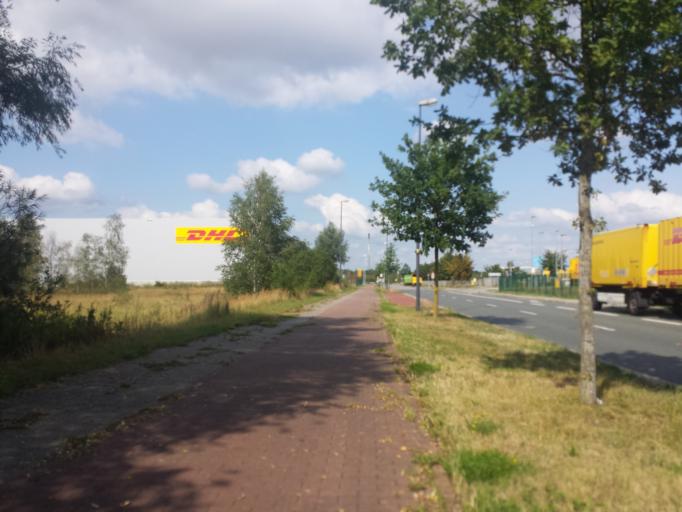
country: DE
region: Lower Saxony
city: Stuhr
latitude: 53.1002
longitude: 8.7040
